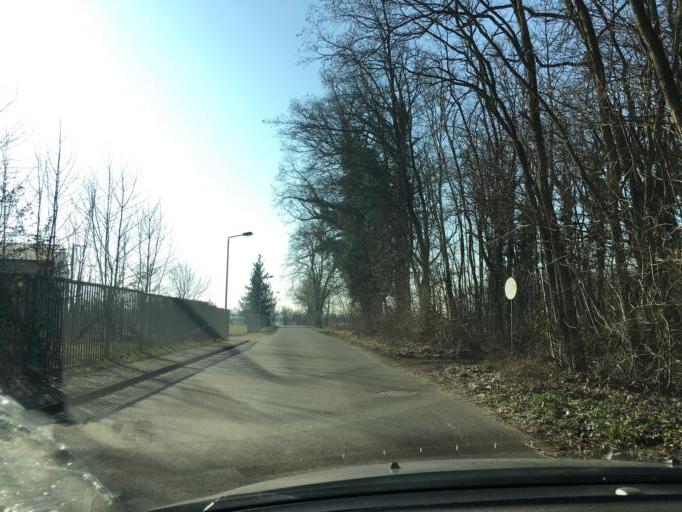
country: DE
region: Saxony
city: Belgershain
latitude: 51.2327
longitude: 12.5529
